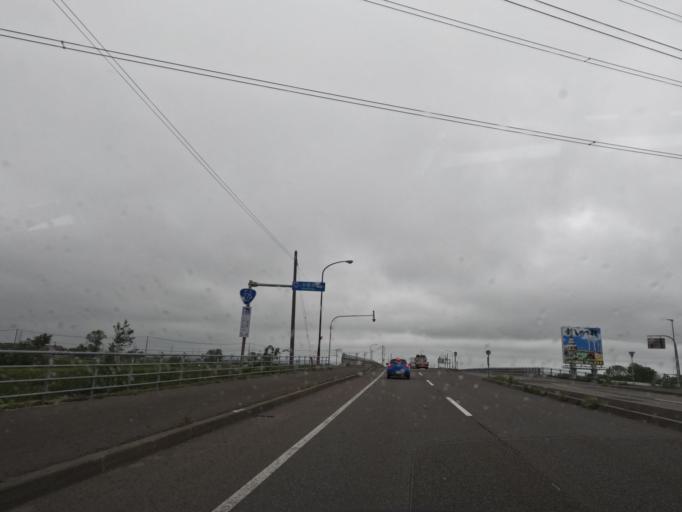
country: JP
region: Hokkaido
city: Tobetsu
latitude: 43.1622
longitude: 141.5197
